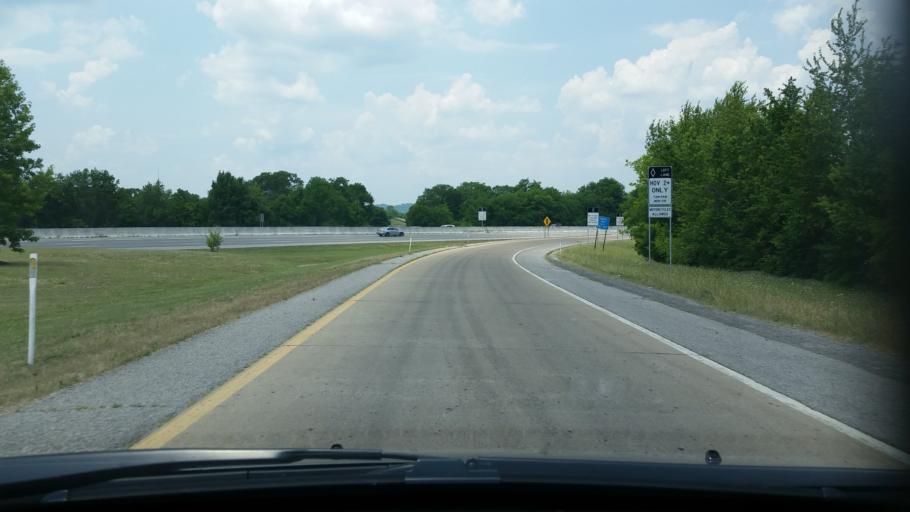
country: US
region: Tennessee
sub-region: Williamson County
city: Brentwood Estates
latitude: 35.9989
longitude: -86.7948
